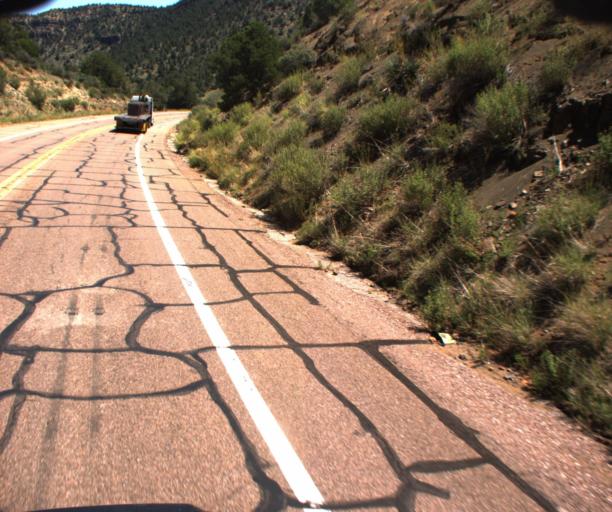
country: US
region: Arizona
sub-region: Navajo County
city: Cibecue
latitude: 33.7726
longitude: -110.5098
